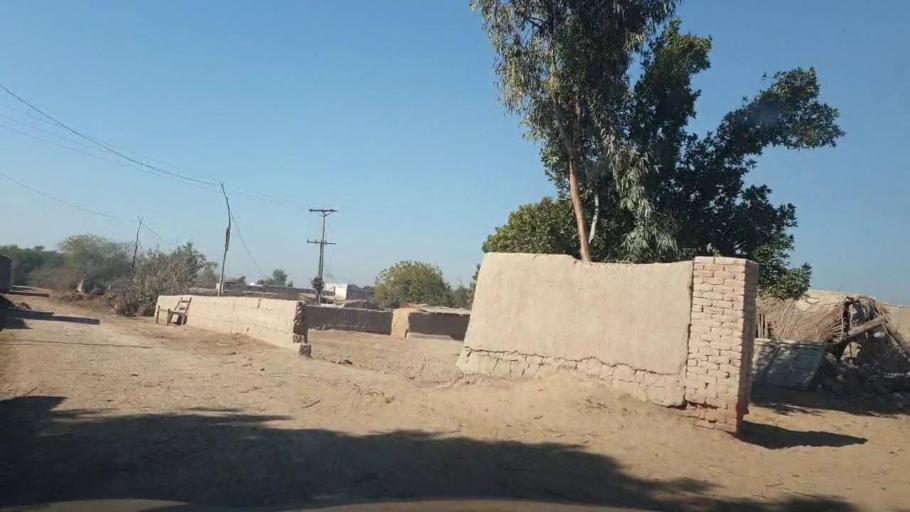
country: PK
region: Sindh
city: Mirpur Mathelo
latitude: 28.0981
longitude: 69.5305
